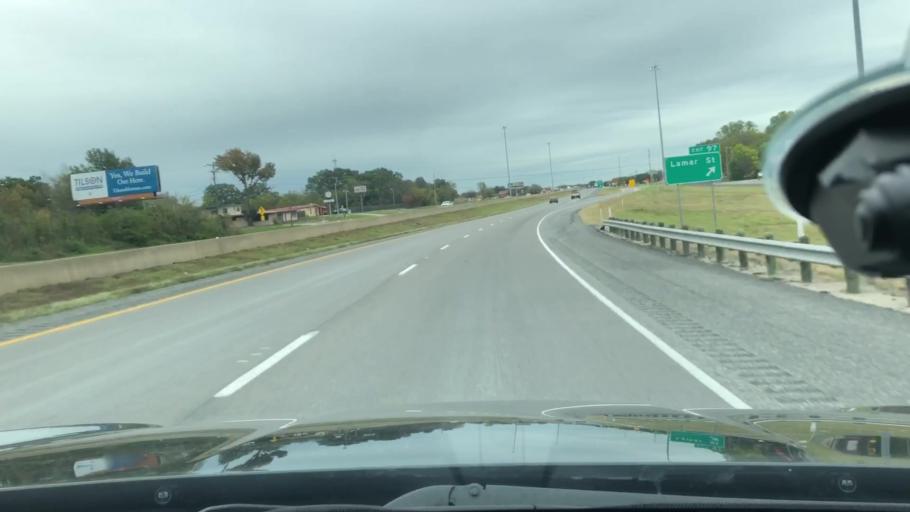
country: US
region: Texas
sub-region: Hunt County
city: Greenville
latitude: 33.1358
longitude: -96.0703
